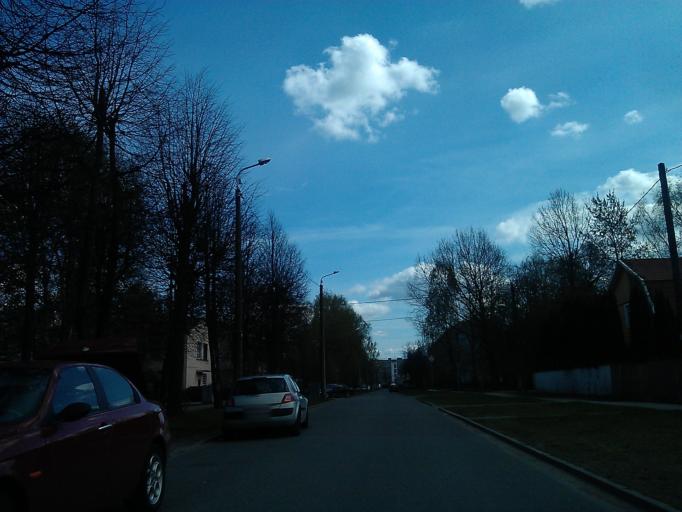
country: LV
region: Kekava
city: Balozi
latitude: 56.9105
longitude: 24.1882
